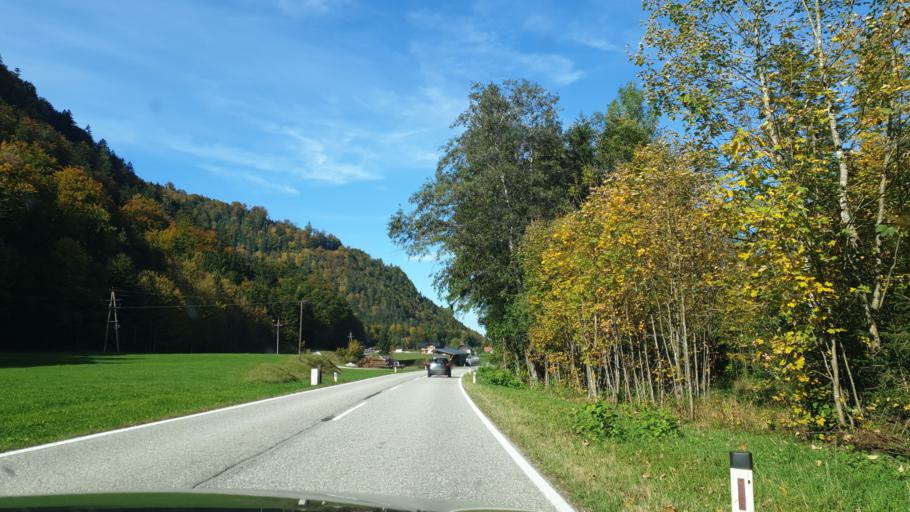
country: AT
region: Salzburg
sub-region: Politischer Bezirk Salzburg-Umgebung
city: Hintersee
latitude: 47.7203
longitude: 13.2813
